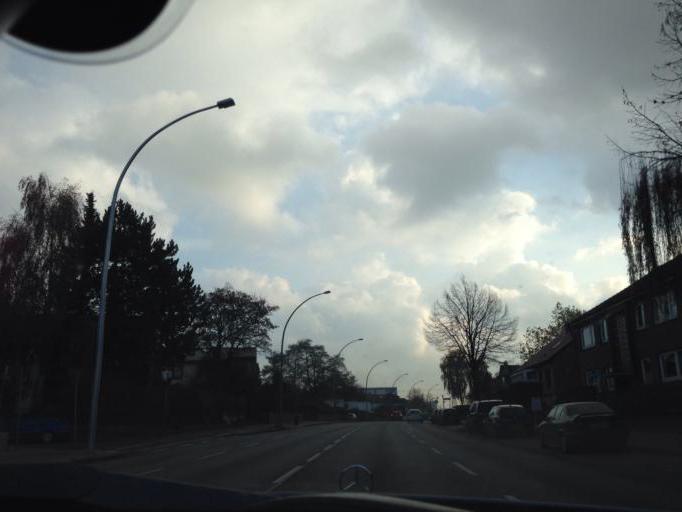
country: DE
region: Hamburg
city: Wandsbek
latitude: 53.5788
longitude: 10.1028
